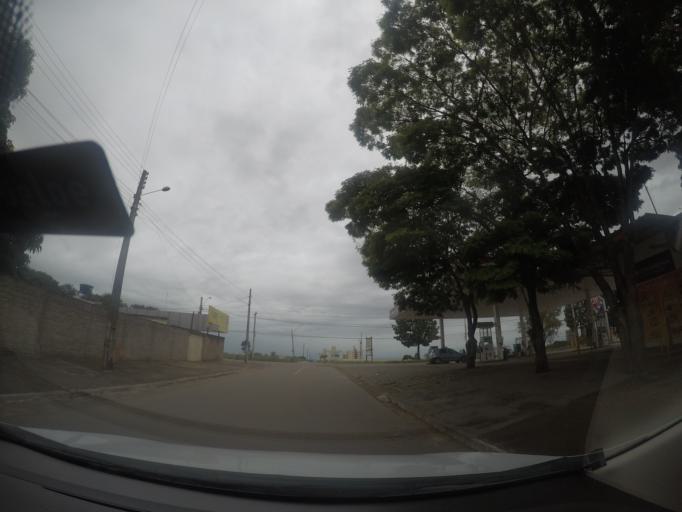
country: BR
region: Goias
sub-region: Goiania
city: Goiania
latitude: -16.7511
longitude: -49.3137
